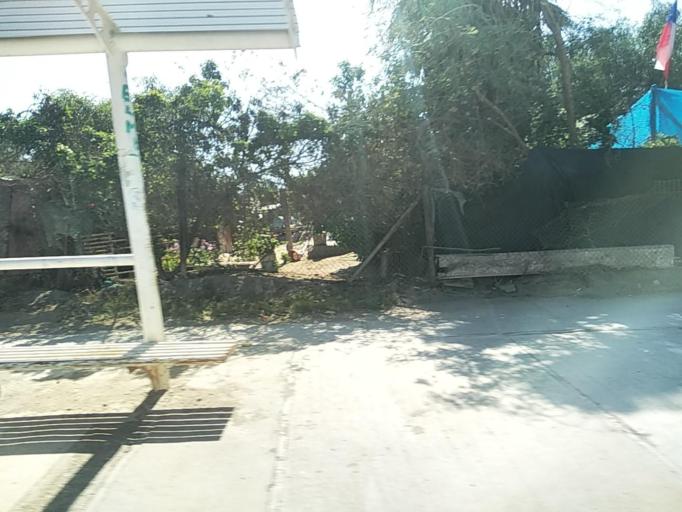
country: CL
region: Atacama
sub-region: Provincia de Copiapo
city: Copiapo
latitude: -27.4037
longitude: -70.2904
